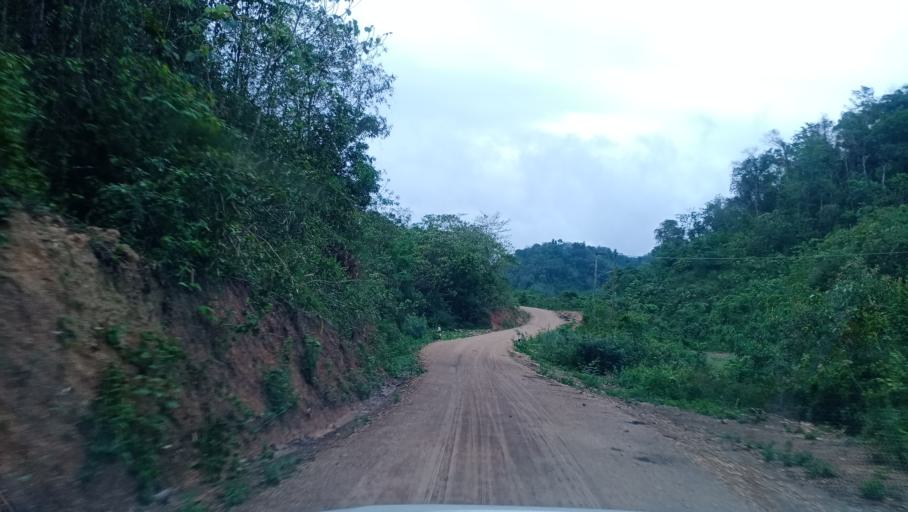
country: LA
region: Phongsali
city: Khoa
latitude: 21.2499
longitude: 102.6948
